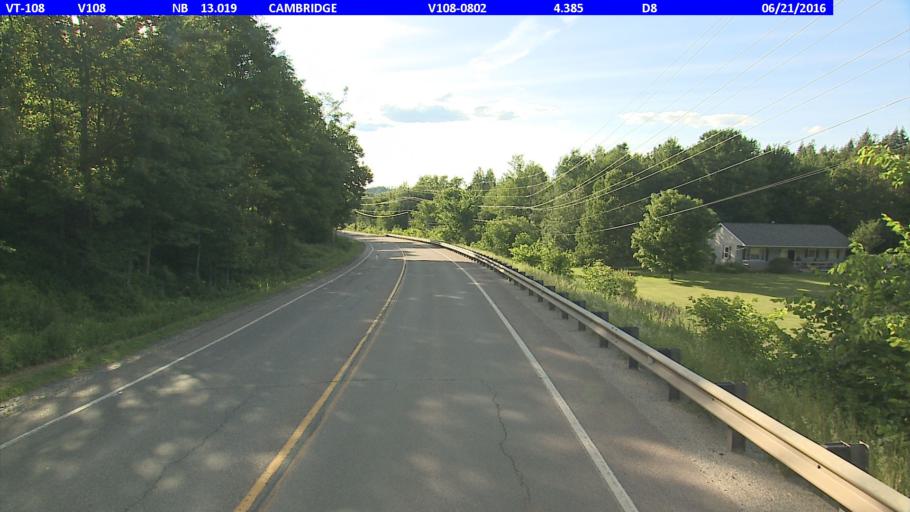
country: US
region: Vermont
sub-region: Lamoille County
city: Johnson
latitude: 44.5923
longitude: -72.7953
